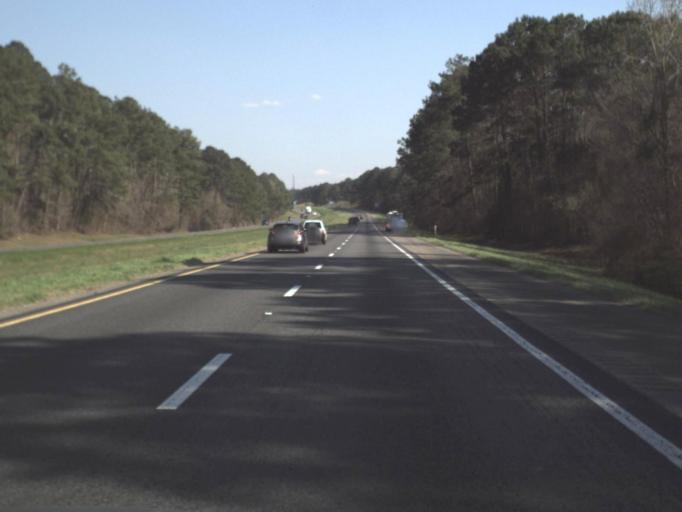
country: US
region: Florida
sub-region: Gadsden County
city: Quincy
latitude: 30.5448
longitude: -84.6129
